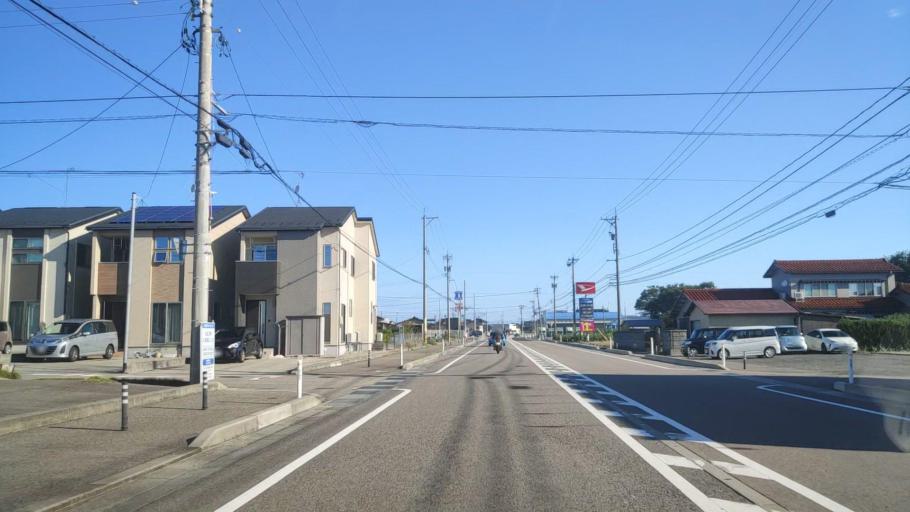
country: JP
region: Ishikawa
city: Tsubata
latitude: 36.7278
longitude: 136.6987
